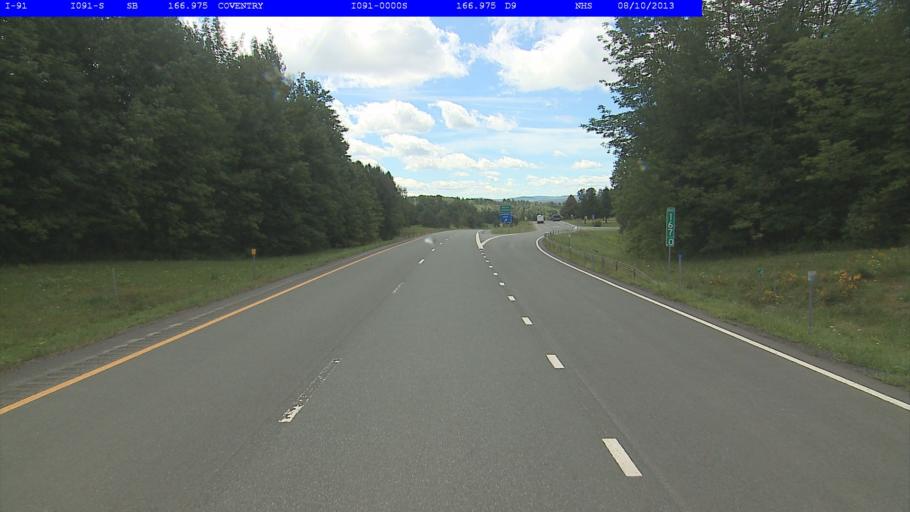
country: US
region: Vermont
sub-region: Orleans County
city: Newport
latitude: 44.8794
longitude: -72.1731
